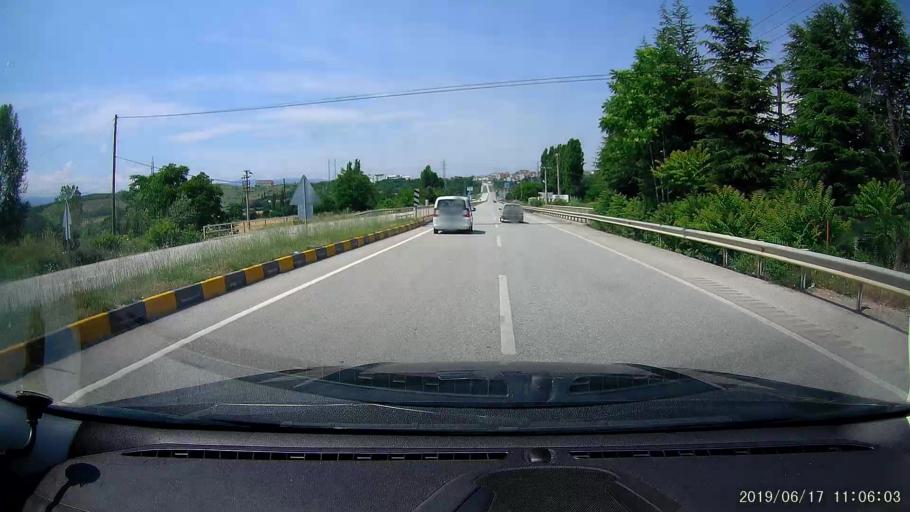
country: TR
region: Kastamonu
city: Tosya
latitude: 41.0164
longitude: 34.0731
